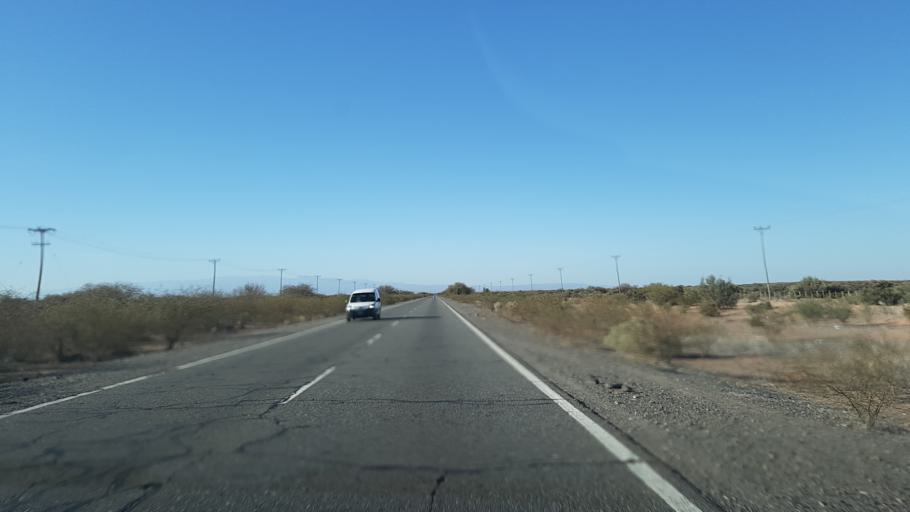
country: AR
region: San Juan
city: Caucete
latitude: -31.6426
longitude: -67.7564
